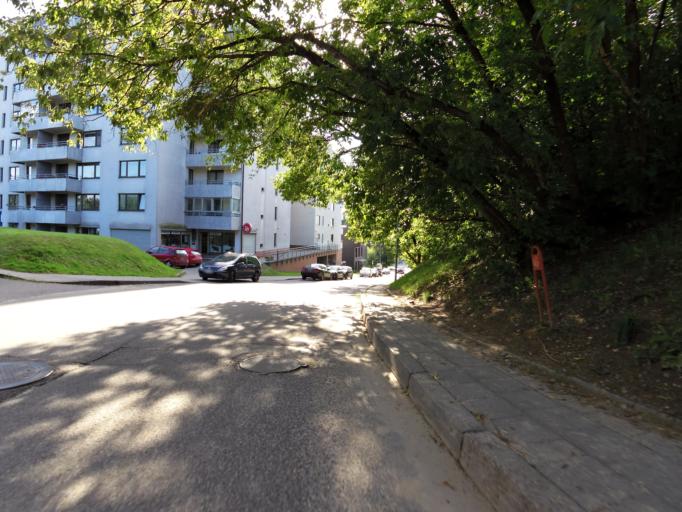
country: LT
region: Vilnius County
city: Rasos
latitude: 54.6852
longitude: 25.3121
